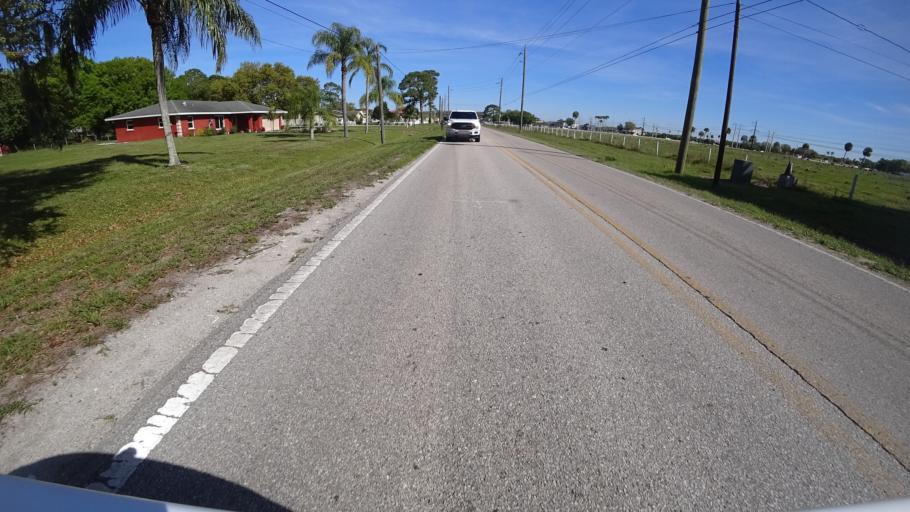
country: US
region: Florida
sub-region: Manatee County
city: Ellenton
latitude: 27.4832
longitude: -82.4569
